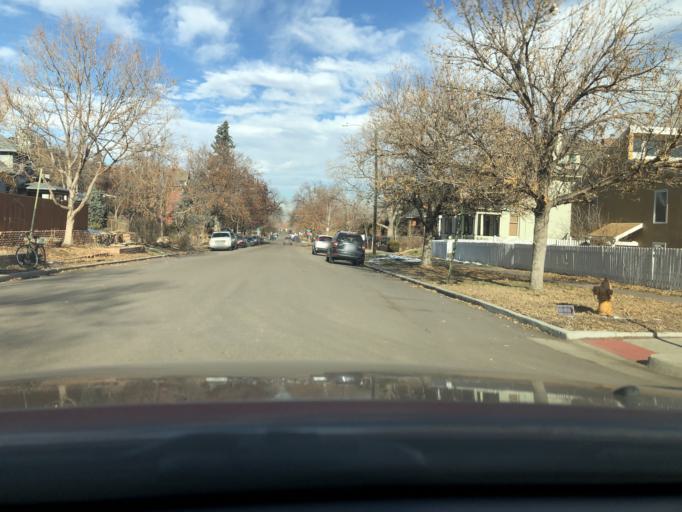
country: US
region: Colorado
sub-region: Denver County
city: Denver
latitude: 39.7495
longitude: -104.9672
